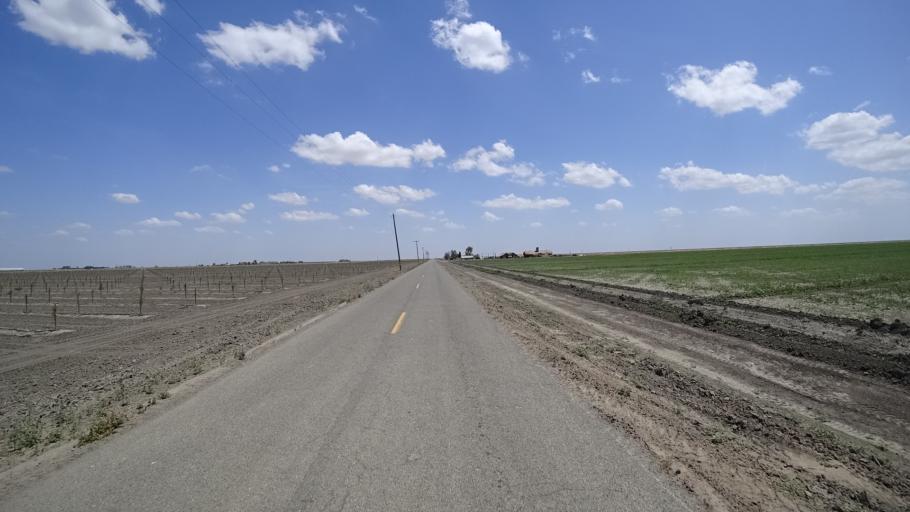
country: US
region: California
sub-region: Kings County
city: Stratford
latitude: 36.1526
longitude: -119.8064
